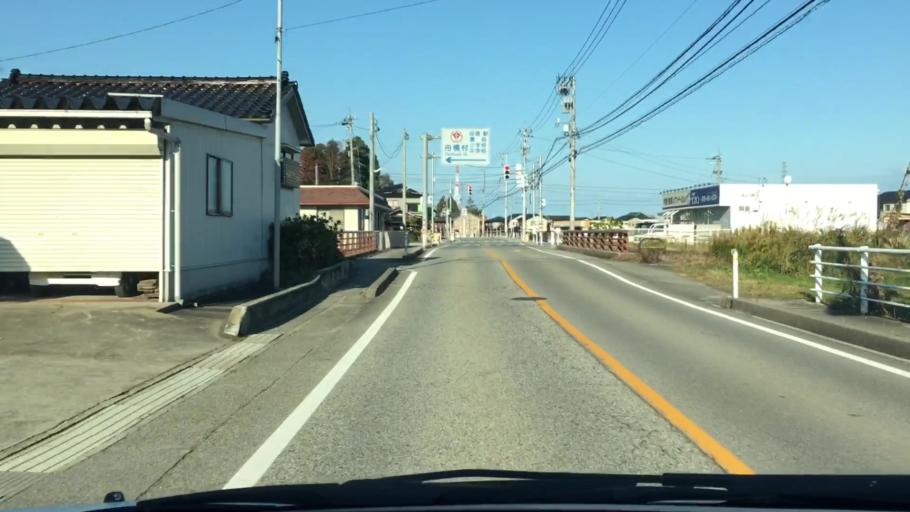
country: JP
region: Toyama
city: Kamiichi
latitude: 36.7056
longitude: 137.3100
